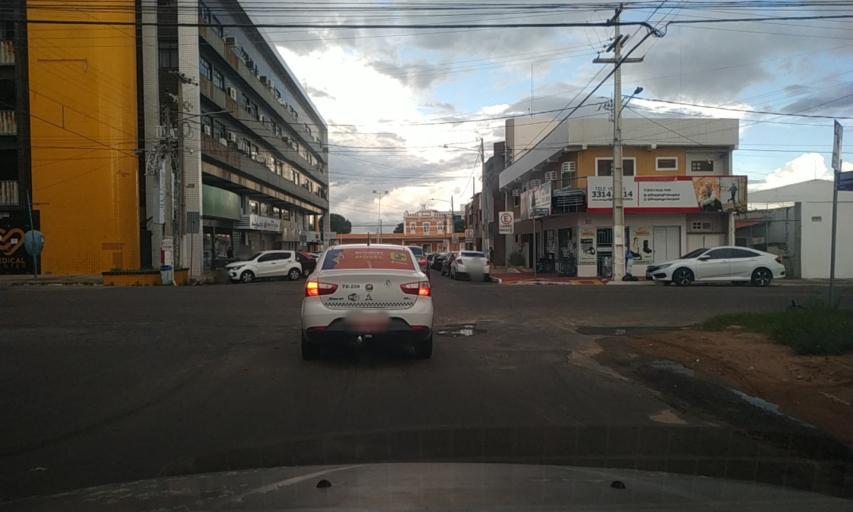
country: BR
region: Rio Grande do Norte
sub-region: Mossoro
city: Mossoro
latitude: -5.1889
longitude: -37.3456
